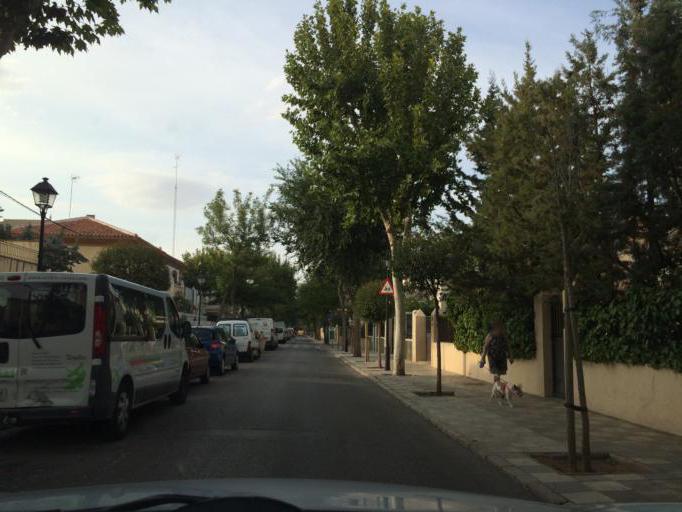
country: ES
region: Castille-La Mancha
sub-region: Provincia de Albacete
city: Albacete
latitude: 38.9912
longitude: -1.8680
